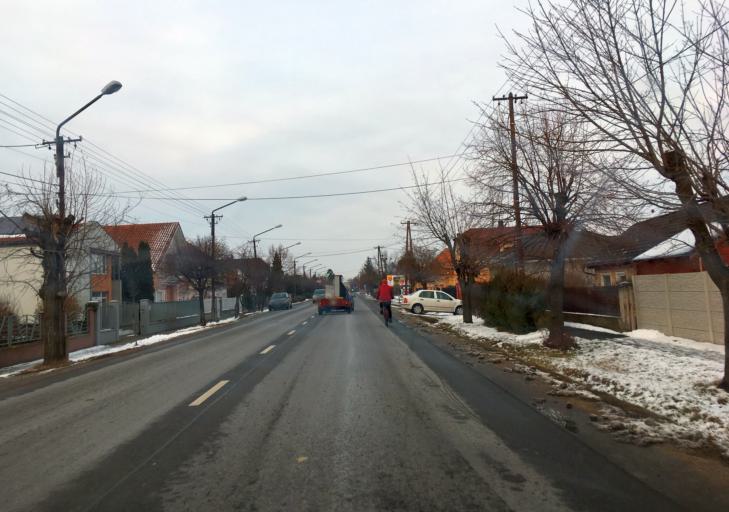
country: HU
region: Gyor-Moson-Sopron
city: Mosonmagyarovar
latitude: 47.8629
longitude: 17.2672
